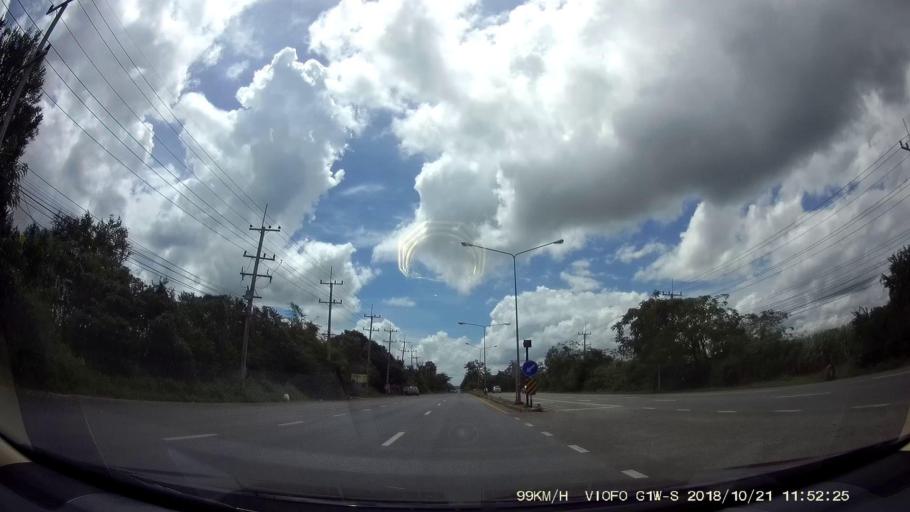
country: TH
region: Chaiyaphum
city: Chatturat
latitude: 15.6098
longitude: 101.9118
